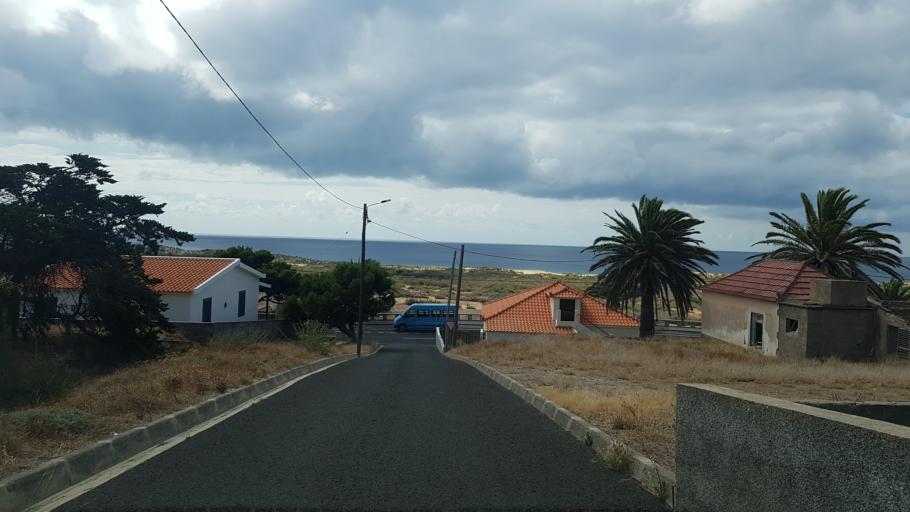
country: PT
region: Madeira
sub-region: Porto Santo
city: Vila de Porto Santo
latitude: 33.0337
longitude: -16.3748
